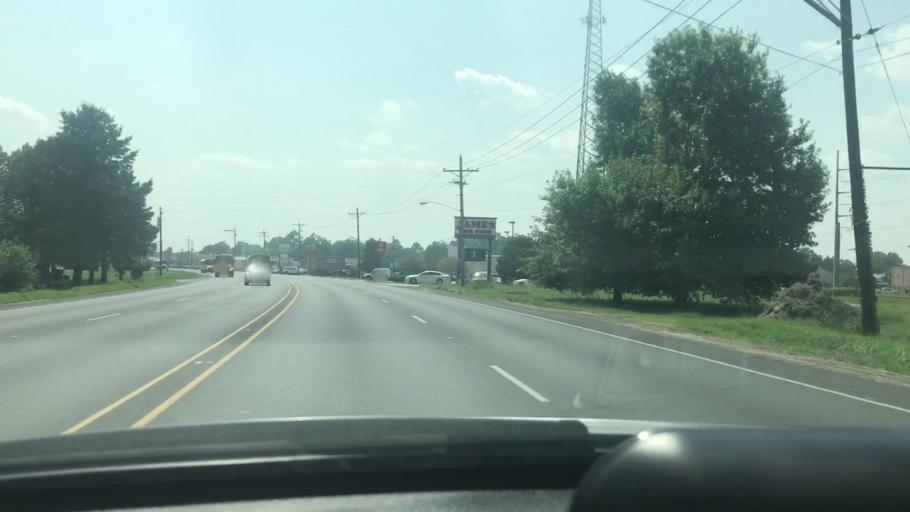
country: US
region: Louisiana
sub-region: Livingston Parish
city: Denham Springs
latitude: 30.4842
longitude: -90.9516
